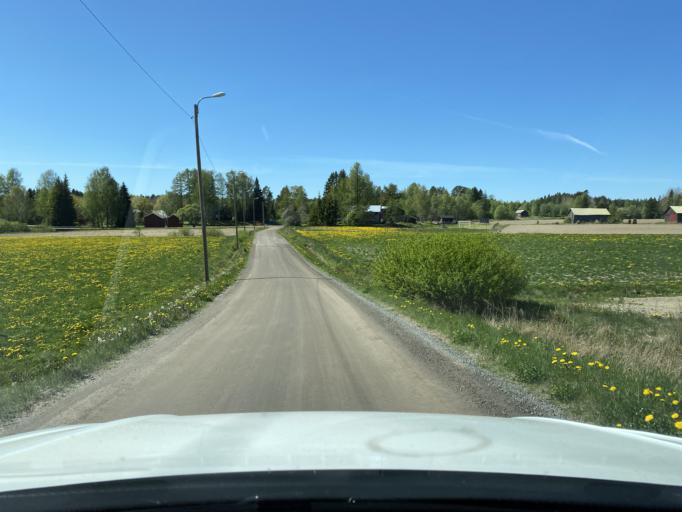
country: FI
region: Satakunta
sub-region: Rauma
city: Lappi
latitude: 61.1393
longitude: 21.9523
